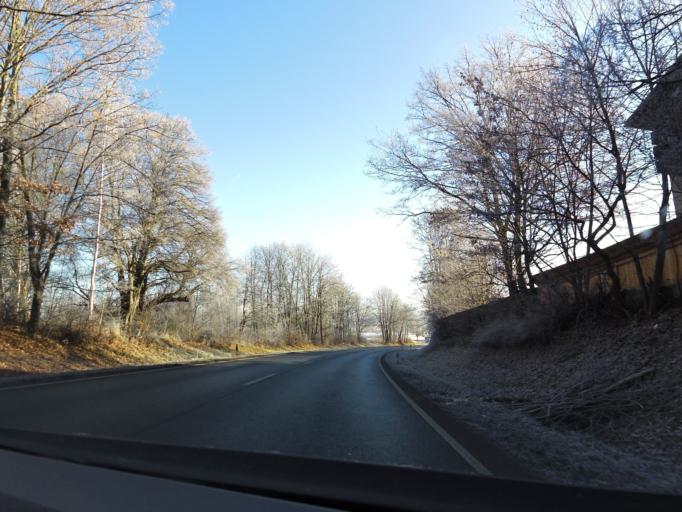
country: DE
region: Bavaria
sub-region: Upper Franconia
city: Marktredwitz
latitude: 50.0157
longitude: 12.0880
